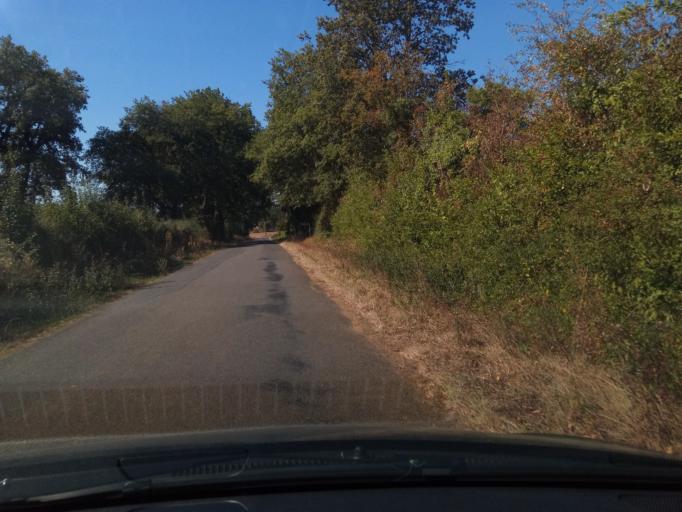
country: FR
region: Poitou-Charentes
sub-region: Departement de la Vienne
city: Montmorillon
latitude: 46.4815
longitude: 0.8538
